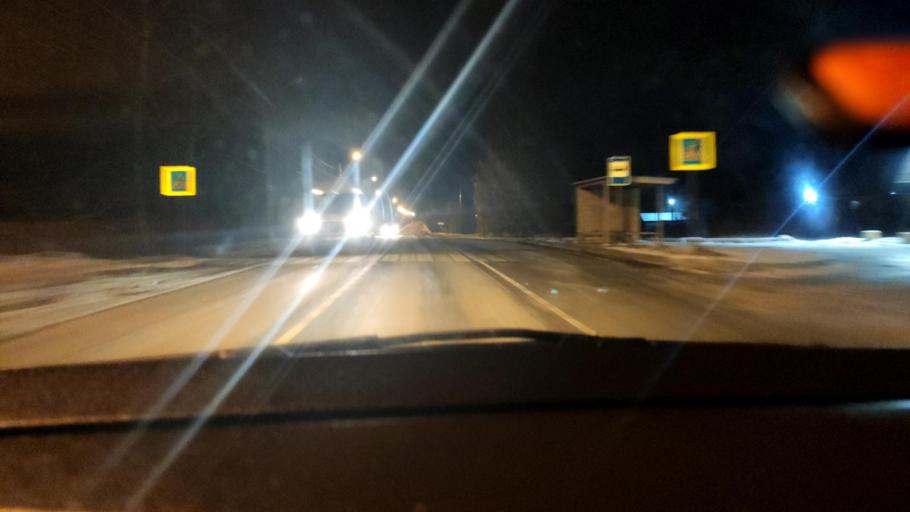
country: RU
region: Voronezj
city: Pridonskoy
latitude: 51.6384
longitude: 39.0884
